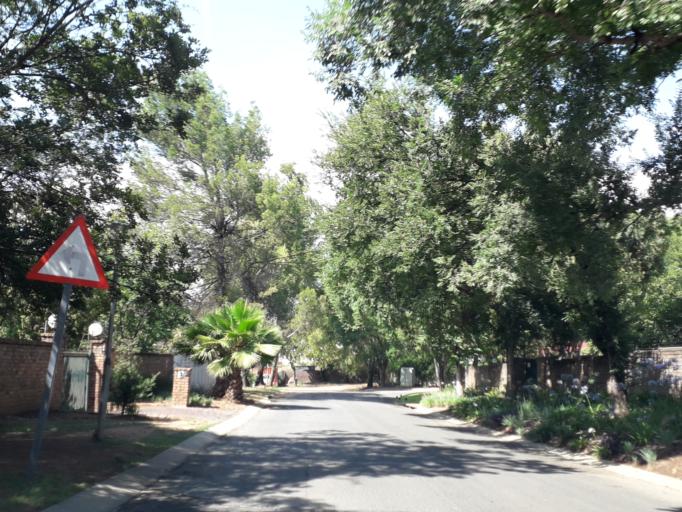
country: ZA
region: Gauteng
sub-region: City of Johannesburg Metropolitan Municipality
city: Midrand
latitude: -26.0408
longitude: 28.0489
